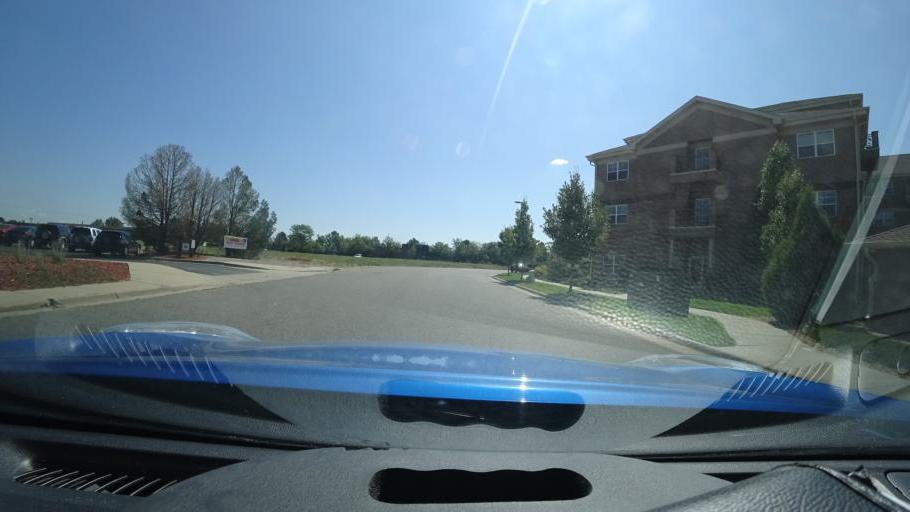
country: US
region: Colorado
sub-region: Adams County
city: Aurora
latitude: 39.6799
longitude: -104.8216
